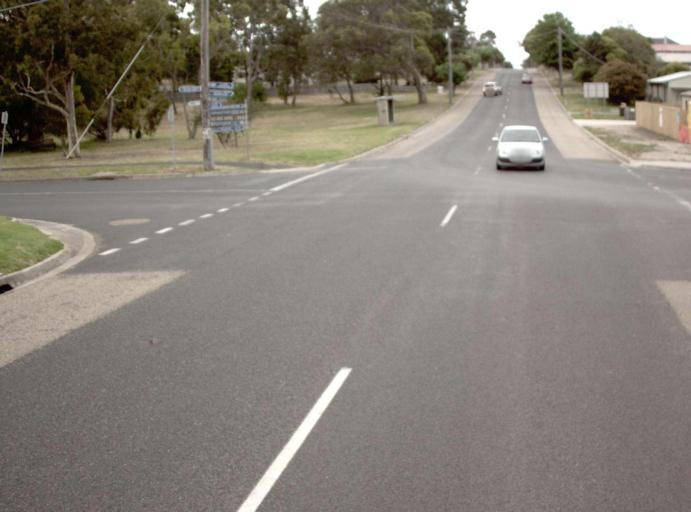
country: AU
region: Victoria
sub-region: East Gippsland
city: Bairnsdale
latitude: -37.9153
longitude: 147.7190
